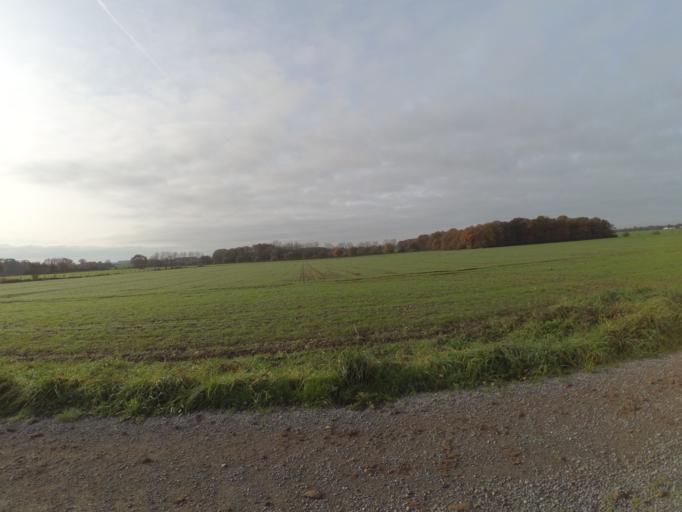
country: FR
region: Pays de la Loire
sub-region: Departement de la Loire-Atlantique
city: La Planche
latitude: 46.9926
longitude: -1.3898
